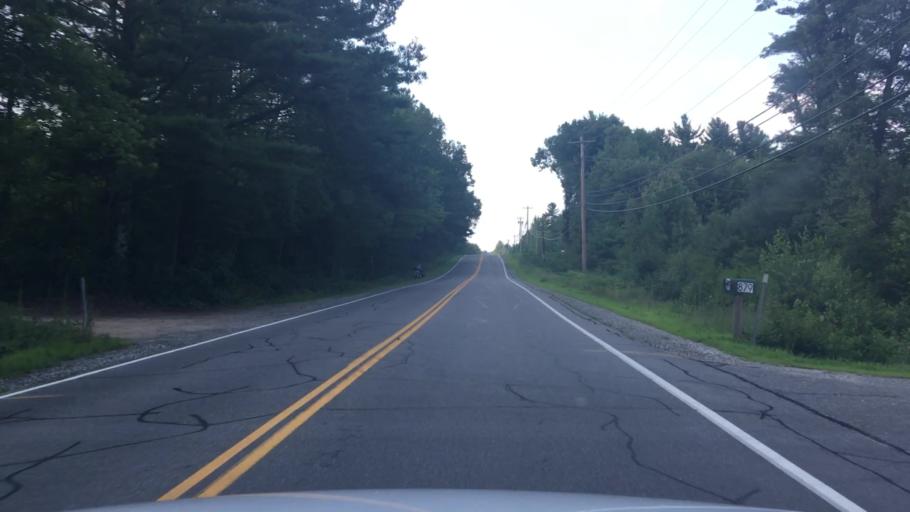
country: US
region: New Hampshire
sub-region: Rockingham County
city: Auburn
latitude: 42.9493
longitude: -71.3515
